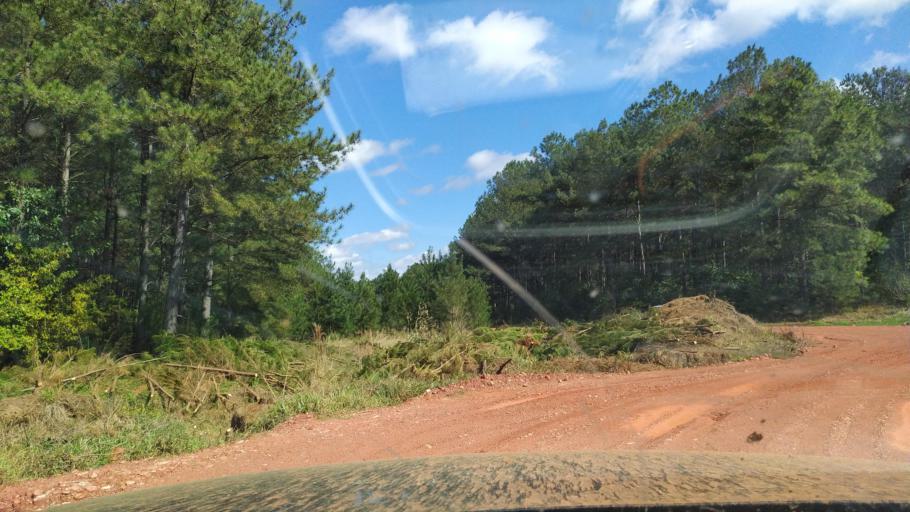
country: AR
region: Corrientes
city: Santo Tome
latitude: -28.4641
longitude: -55.9901
